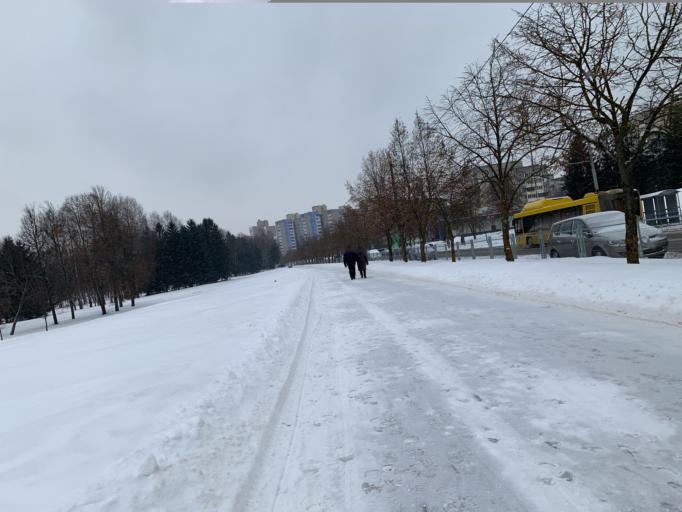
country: BY
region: Minsk
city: Borovlyany
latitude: 53.9536
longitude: 27.6298
